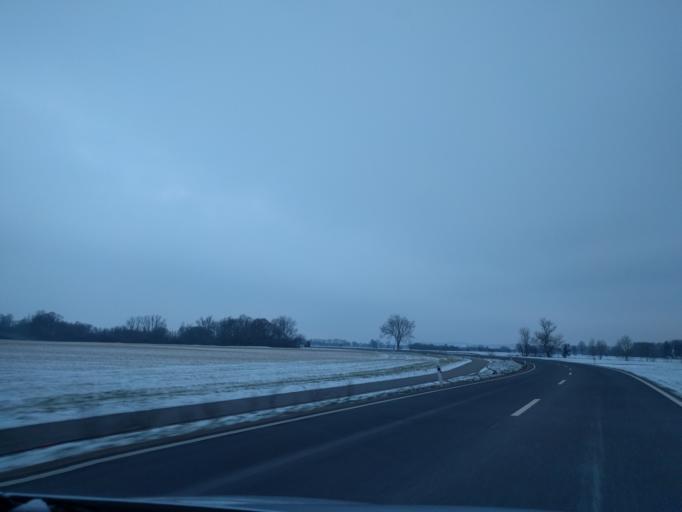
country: DE
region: Bavaria
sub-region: Swabia
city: Asbach-Baumenheim
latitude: 48.7104
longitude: 10.8337
